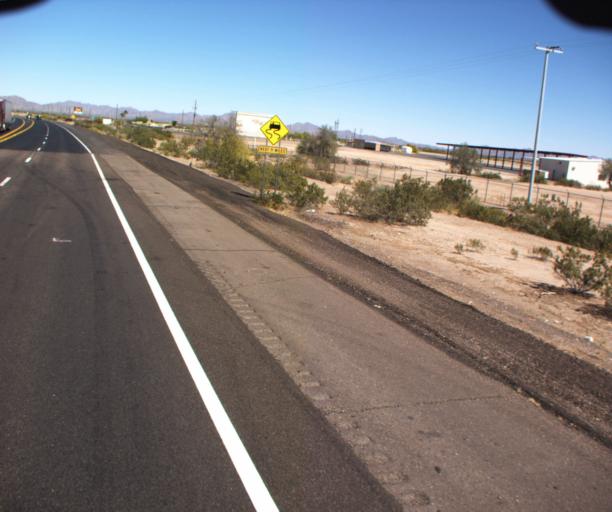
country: US
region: Arizona
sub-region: Maricopa County
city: Gila Bend
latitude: 32.9585
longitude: -112.6821
